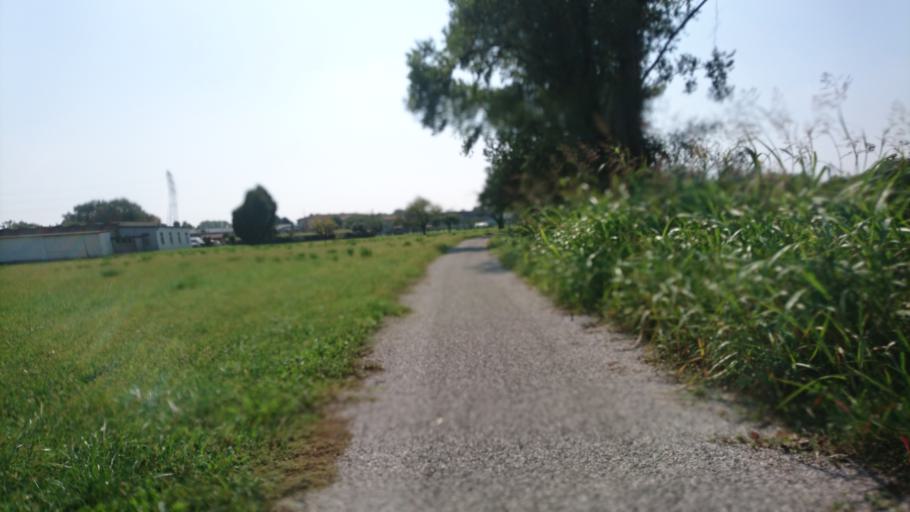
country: IT
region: Veneto
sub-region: Provincia di Padova
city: Piazzola sul Brenta
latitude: 45.5452
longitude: 11.8051
